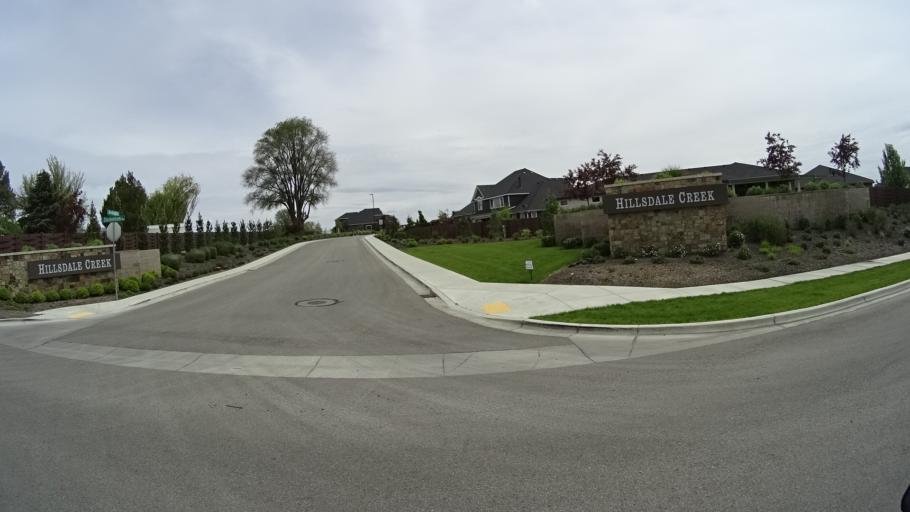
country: US
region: Idaho
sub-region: Ada County
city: Meridian
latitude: 43.5574
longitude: -116.3444
